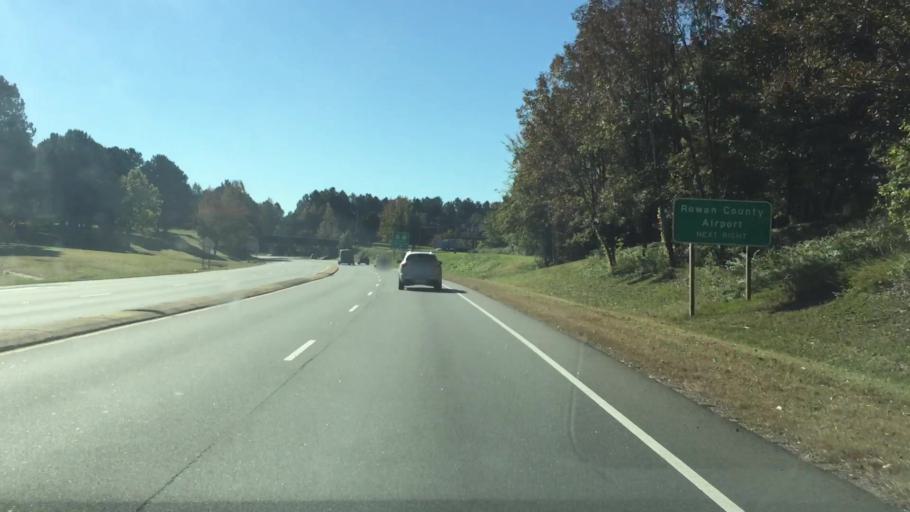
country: US
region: North Carolina
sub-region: Rowan County
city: Salisbury
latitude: 35.6542
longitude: -80.5000
